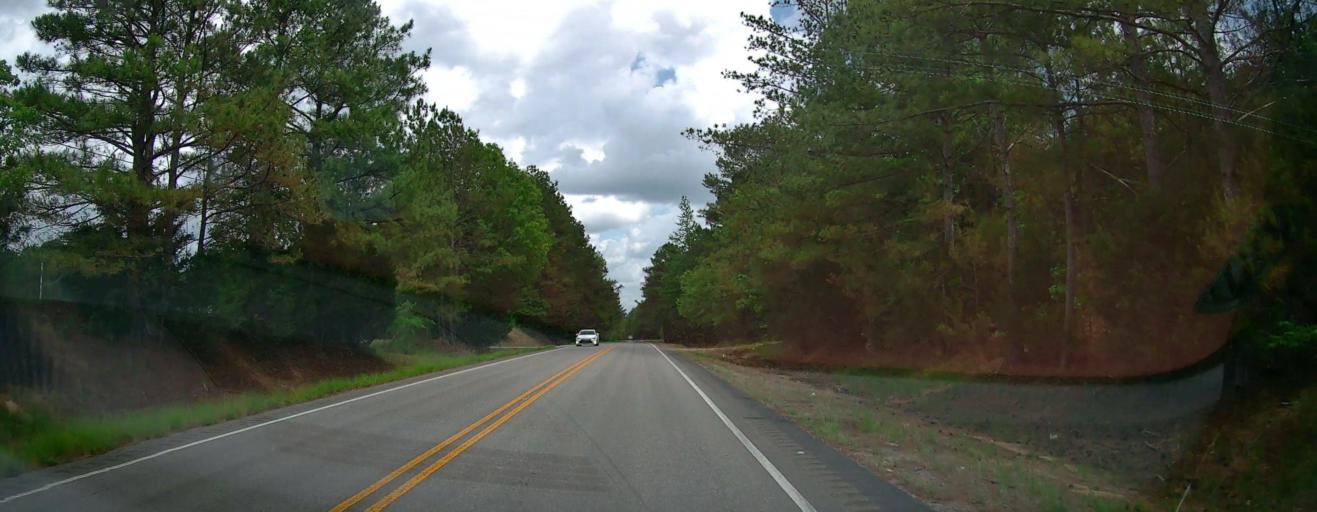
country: US
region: Alabama
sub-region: Marion County
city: Hamilton
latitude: 34.1234
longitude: -88.0386
